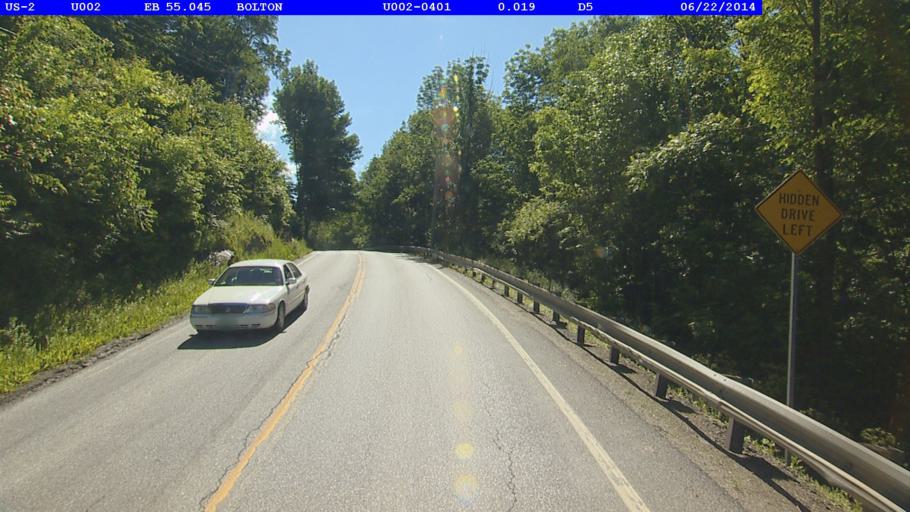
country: US
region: Vermont
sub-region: Chittenden County
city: Jericho
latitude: 44.3824
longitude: -72.9333
